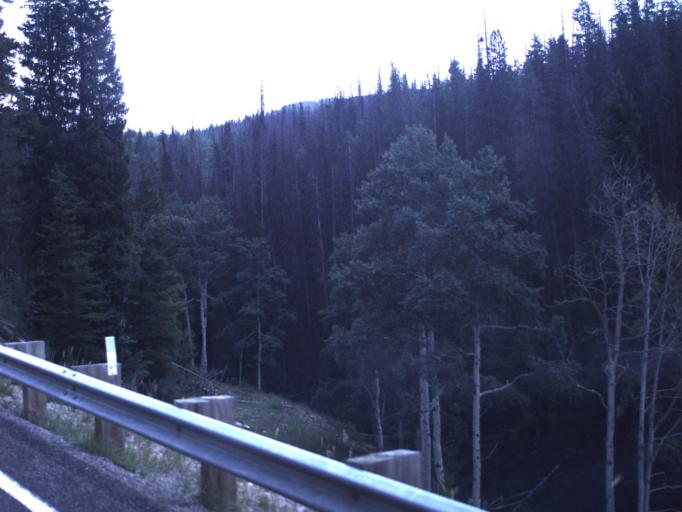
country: US
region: Utah
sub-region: Summit County
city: Francis
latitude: 40.5172
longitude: -111.0508
